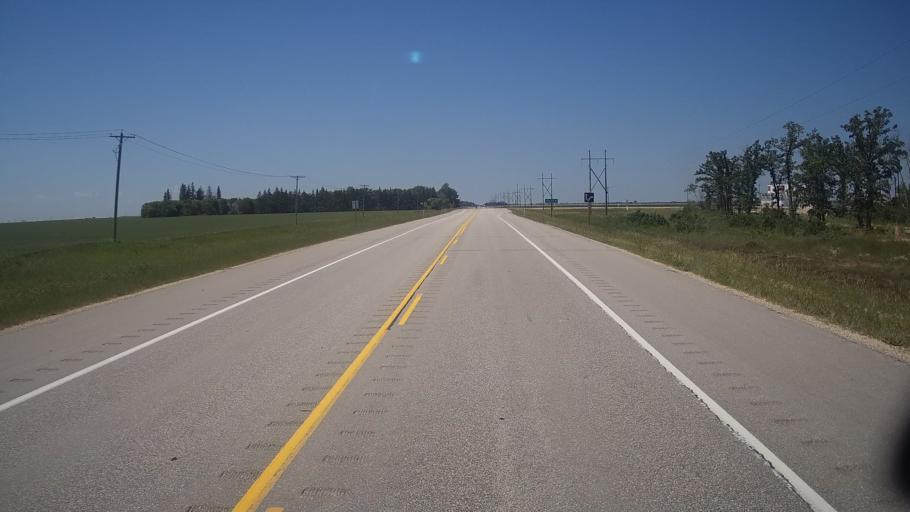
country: CA
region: Manitoba
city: Stonewall
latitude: 50.1230
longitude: -97.5390
